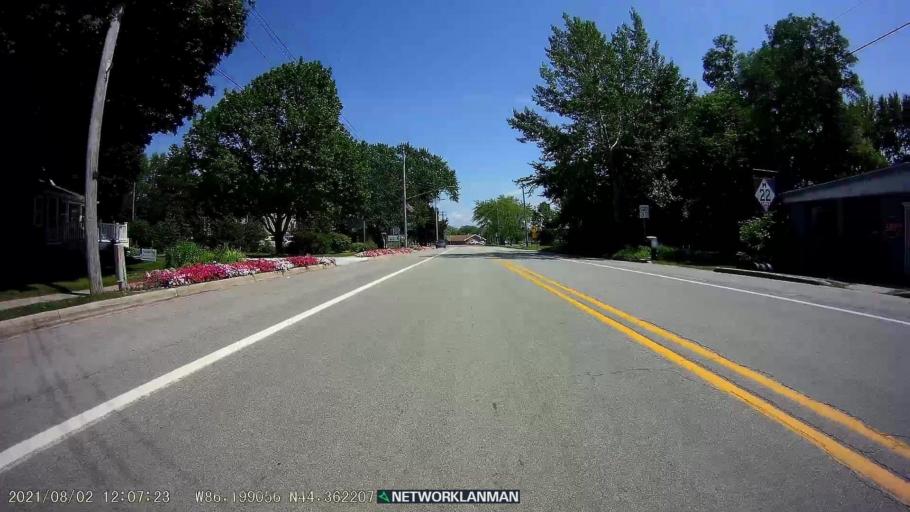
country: US
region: Michigan
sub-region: Manistee County
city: Manistee
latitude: 44.3622
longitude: -86.1991
